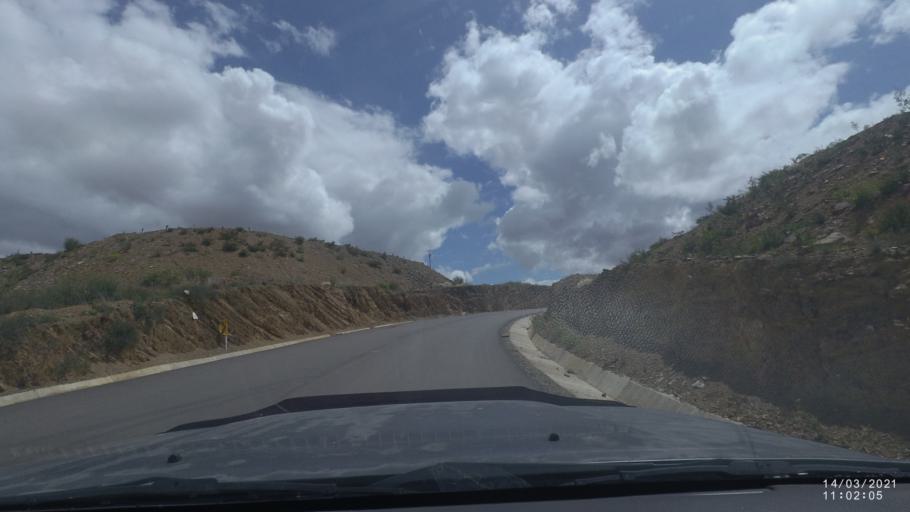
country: BO
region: Cochabamba
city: Tarata
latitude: -17.7874
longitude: -65.9639
